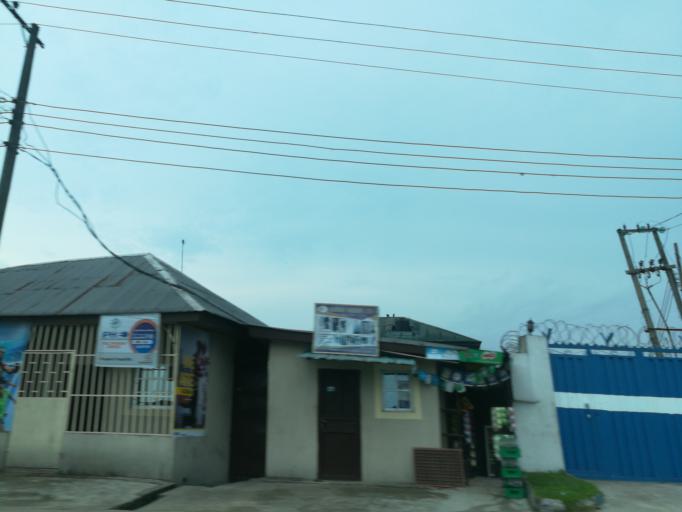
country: NG
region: Rivers
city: Port Harcourt
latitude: 4.8050
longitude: 7.0184
